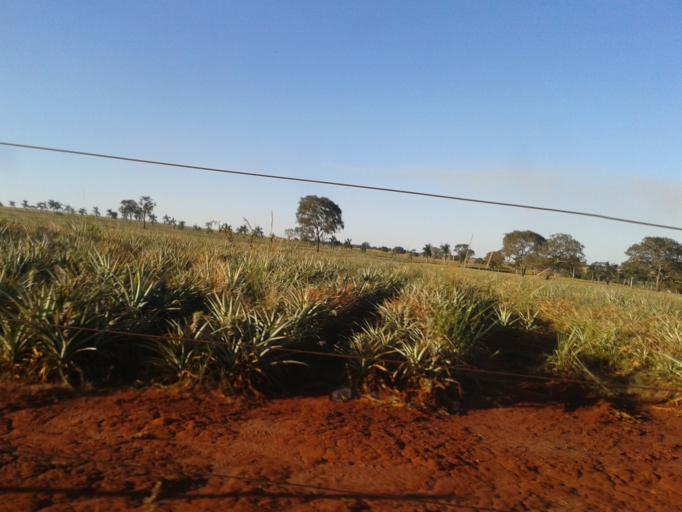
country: BR
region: Minas Gerais
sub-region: Centralina
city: Centralina
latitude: -18.7607
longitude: -49.2010
